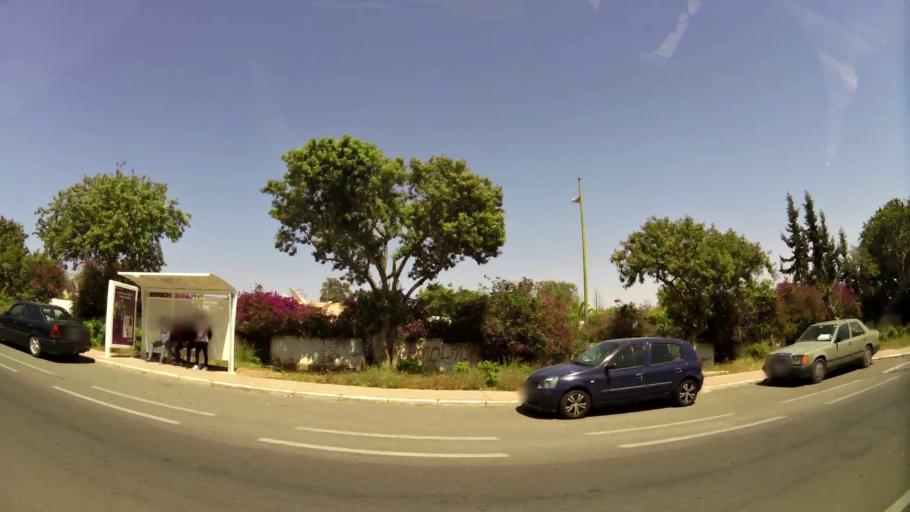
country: MA
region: Souss-Massa-Draa
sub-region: Agadir-Ida-ou-Tnan
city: Agadir
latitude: 30.4347
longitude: -9.5954
